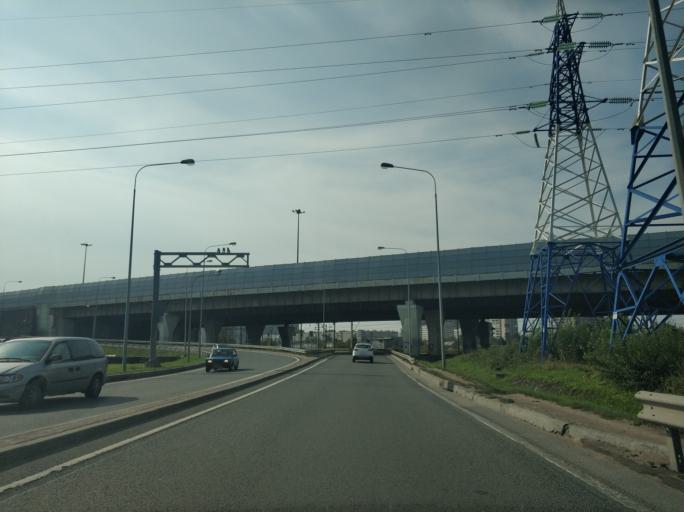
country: RU
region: Leningrad
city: Murino
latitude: 60.0412
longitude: 30.4397
